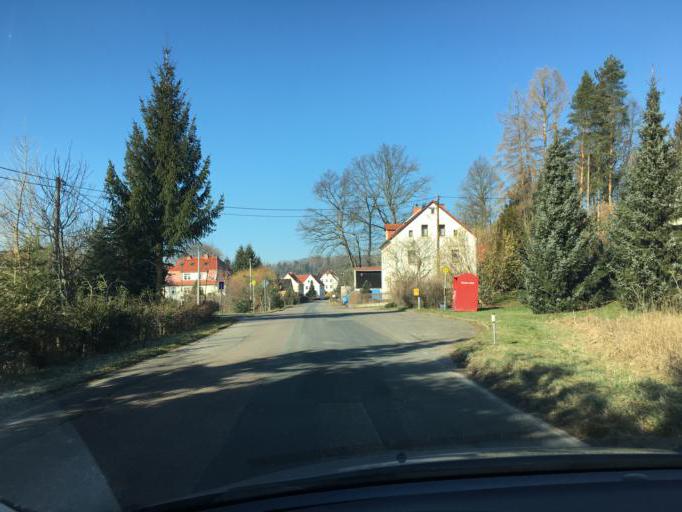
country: DE
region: Saxony
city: Lunzenau
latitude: 50.9640
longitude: 12.7363
